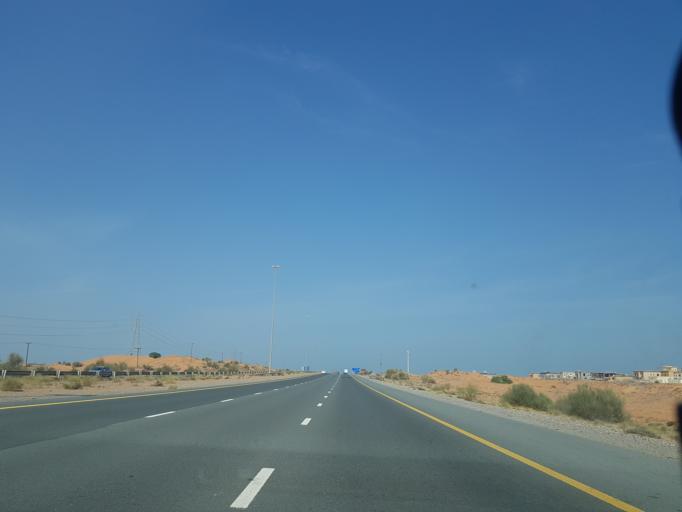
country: AE
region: Ra's al Khaymah
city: Ras al-Khaimah
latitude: 25.6883
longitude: 55.8809
